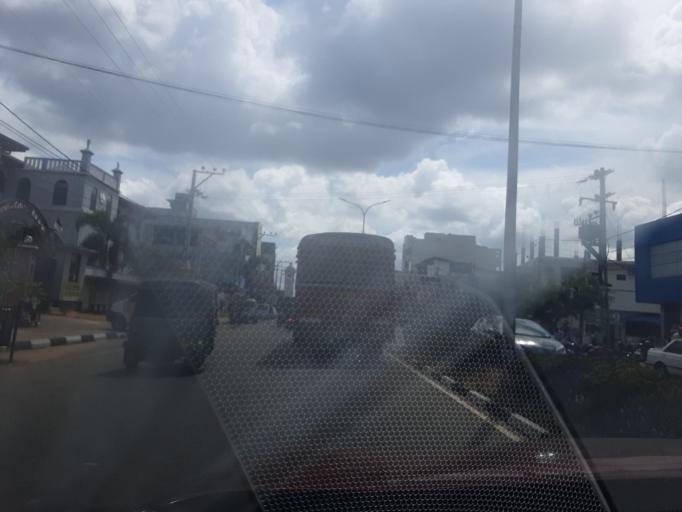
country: LK
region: North Western
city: Kuliyapitiya
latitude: 7.4690
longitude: 80.0395
